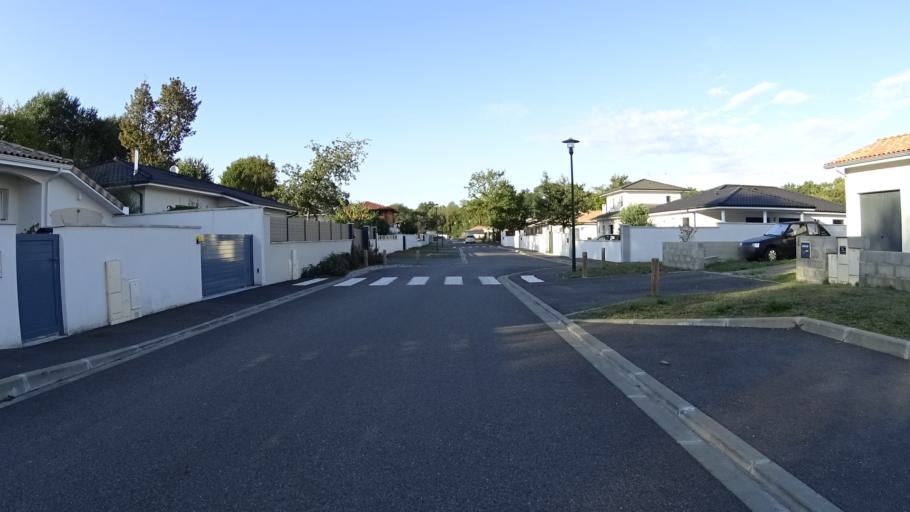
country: FR
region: Aquitaine
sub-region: Departement des Landes
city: Saint-Paul-les-Dax
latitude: 43.7399
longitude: -1.0468
